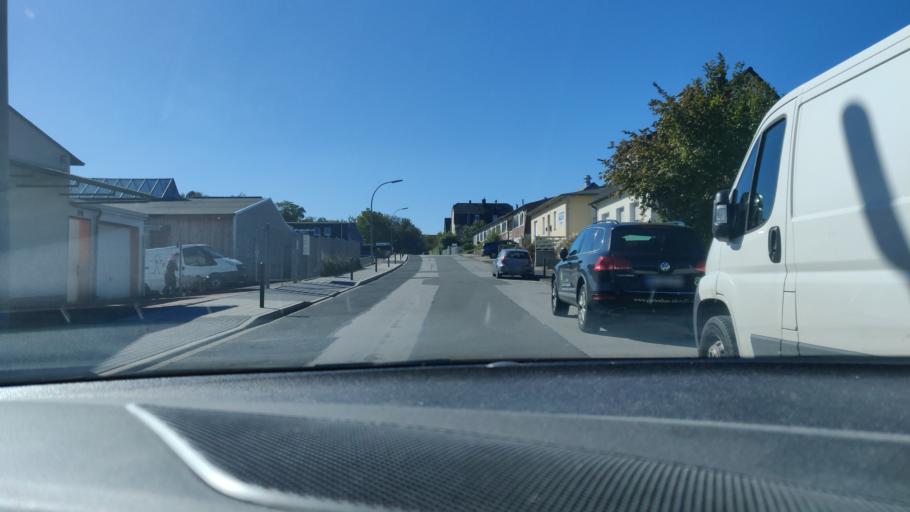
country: DE
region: North Rhine-Westphalia
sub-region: Regierungsbezirk Dusseldorf
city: Velbert
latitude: 51.3410
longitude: 7.0660
